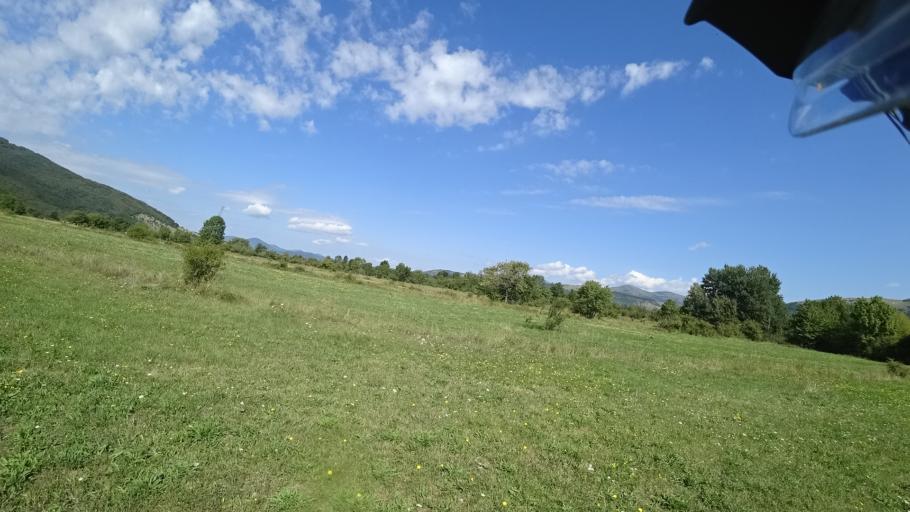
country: HR
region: Zadarska
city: Gracac
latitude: 44.3378
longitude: 15.9541
